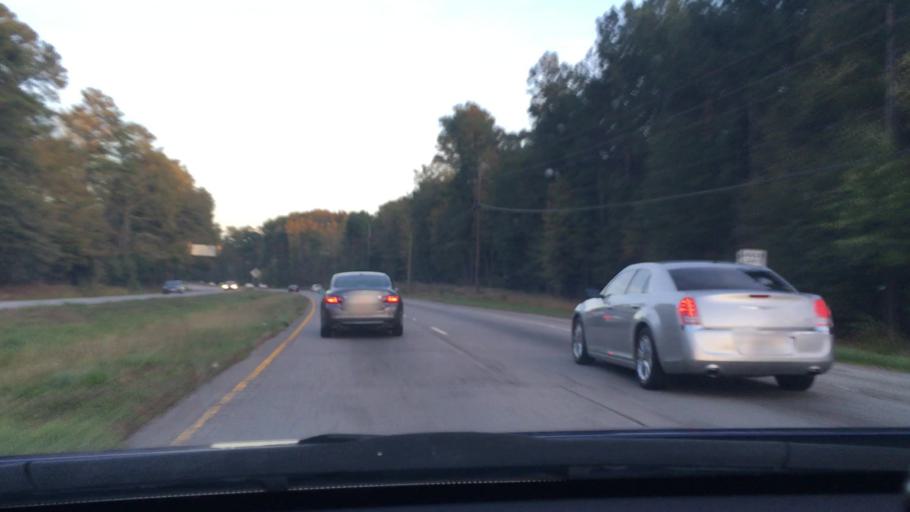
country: US
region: South Carolina
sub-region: Richland County
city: Hopkins
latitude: 33.9440
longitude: -80.9022
